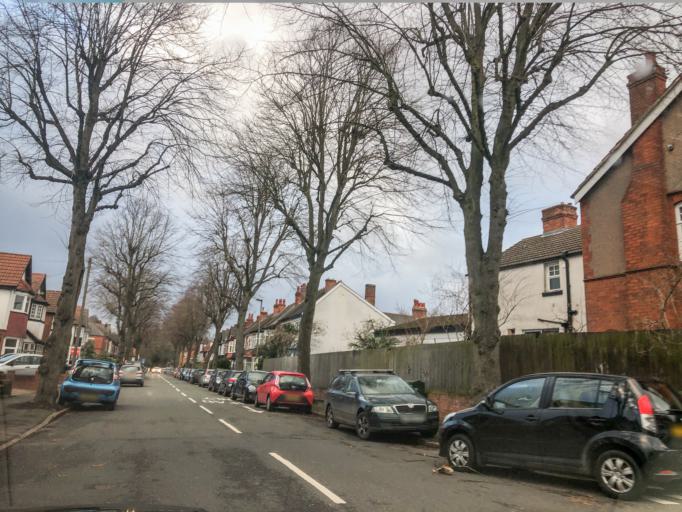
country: GB
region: England
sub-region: City and Borough of Birmingham
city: Birmingham
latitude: 52.4301
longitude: -1.8953
